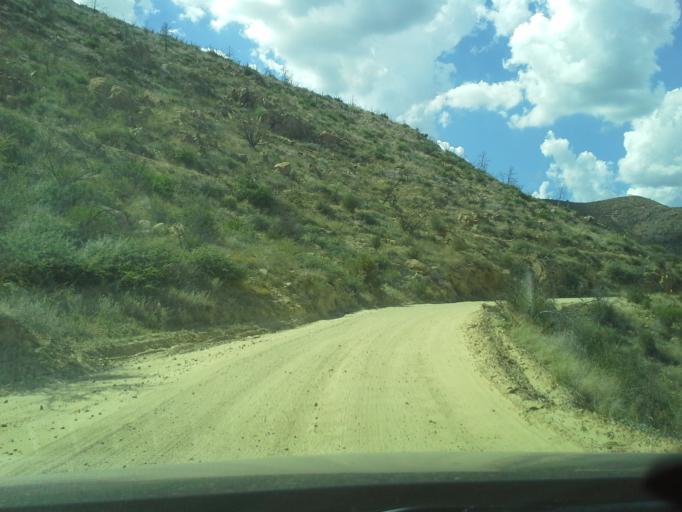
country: US
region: Arizona
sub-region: Yavapai County
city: Mayer
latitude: 34.2533
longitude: -112.3025
